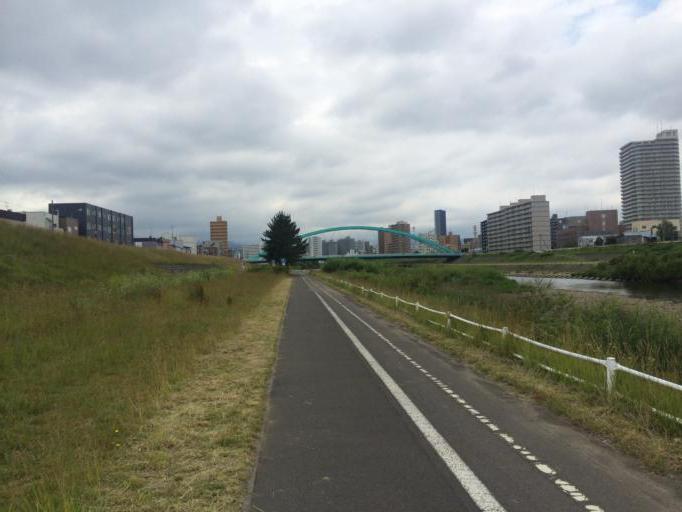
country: JP
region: Hokkaido
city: Sapporo
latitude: 43.0644
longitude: 141.3784
